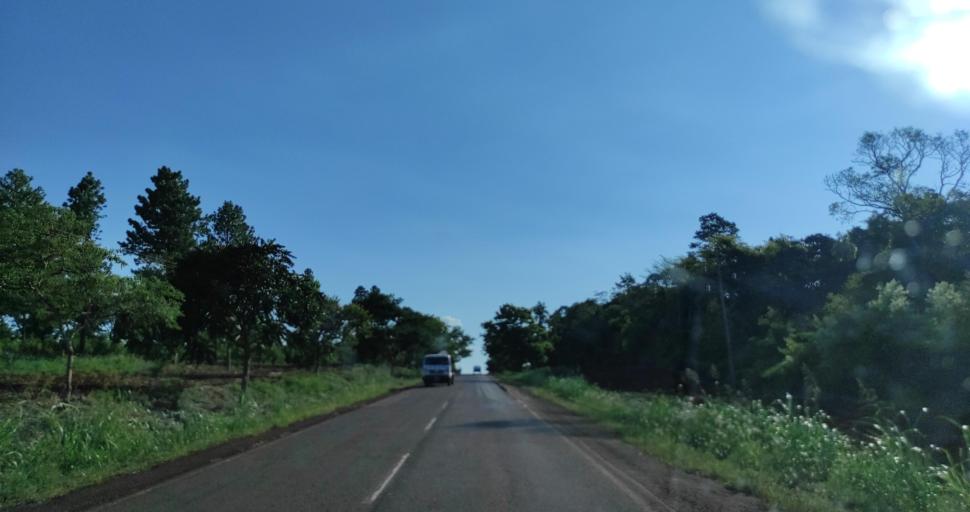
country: AR
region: Misiones
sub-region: Departamento de Eldorado
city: Eldorado
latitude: -26.4039
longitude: -54.4733
